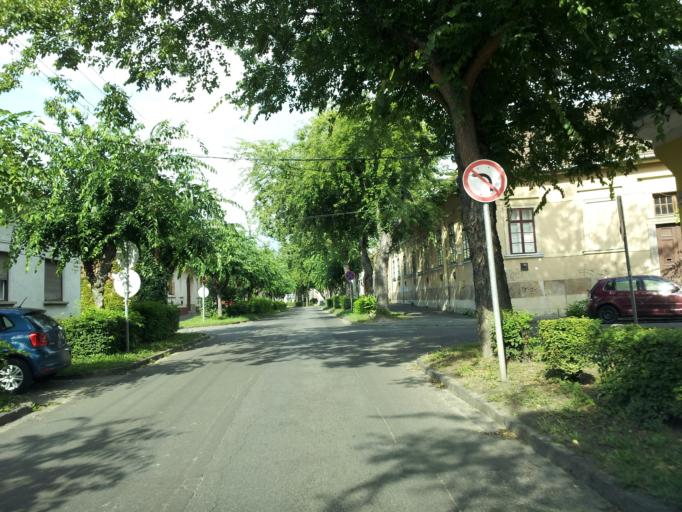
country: HU
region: Pest
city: Vac
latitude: 47.7768
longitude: 19.1328
